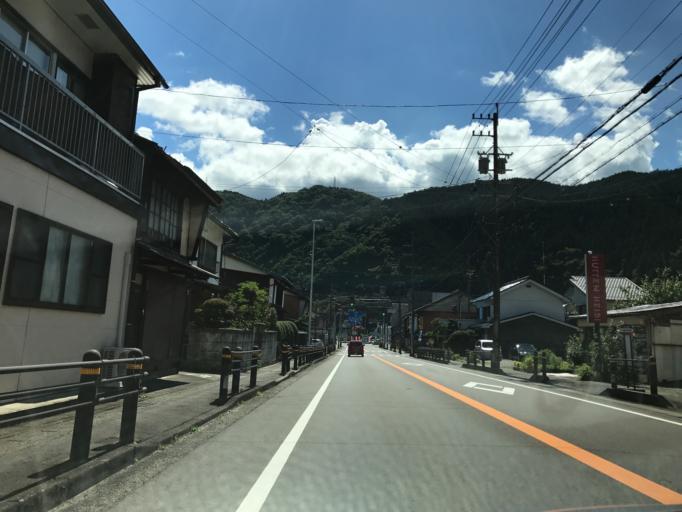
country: JP
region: Gifu
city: Gujo
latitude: 35.7450
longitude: 136.9503
